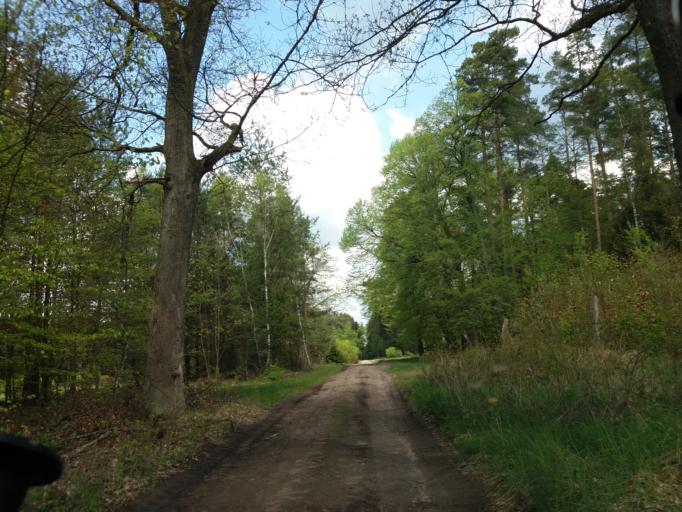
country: PL
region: West Pomeranian Voivodeship
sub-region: Powiat walecki
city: Czlopa
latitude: 53.1201
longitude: 15.9592
